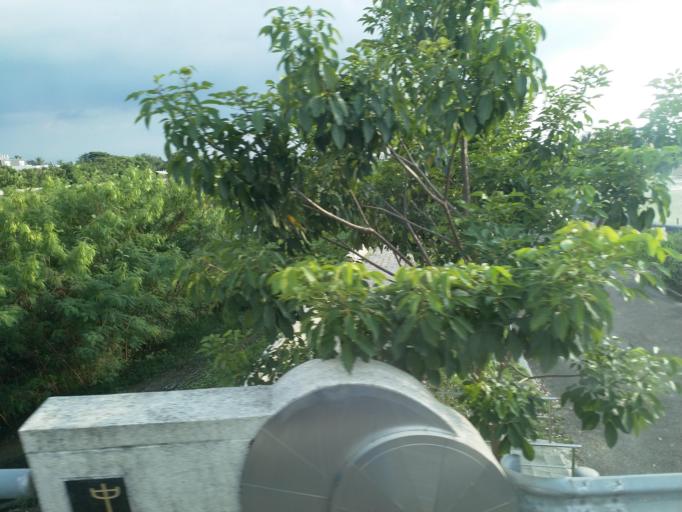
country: TW
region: Taiwan
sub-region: Pingtung
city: Pingtung
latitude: 22.8864
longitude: 120.5243
